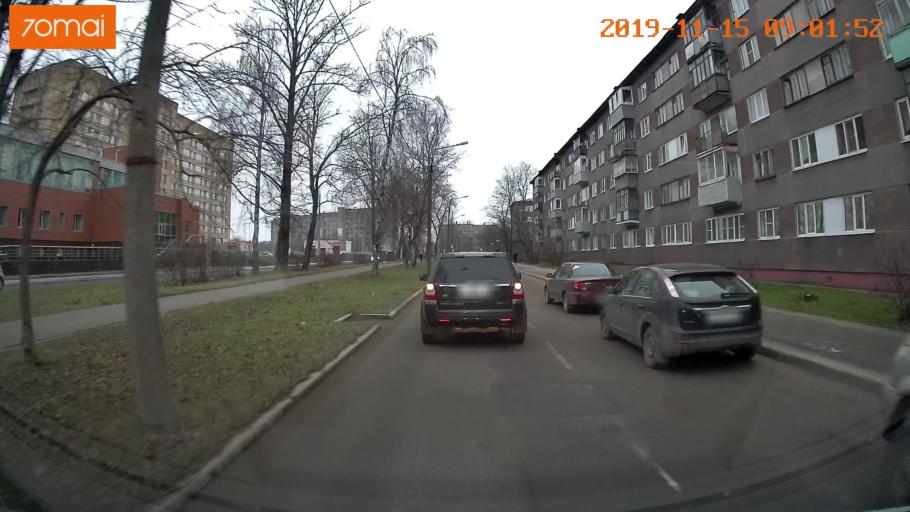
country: RU
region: Vologda
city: Cherepovets
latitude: 59.1345
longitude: 37.9268
